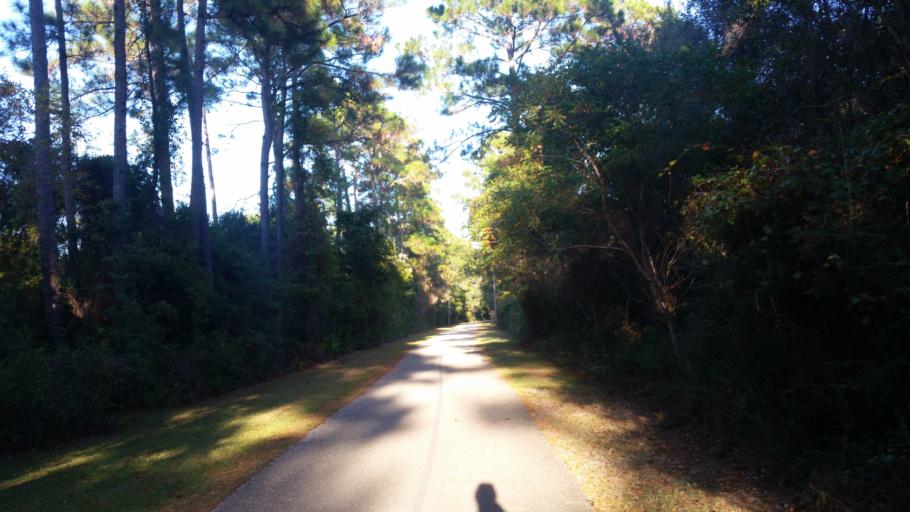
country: US
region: Alabama
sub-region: Baldwin County
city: Orange Beach
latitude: 30.2770
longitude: -87.5939
